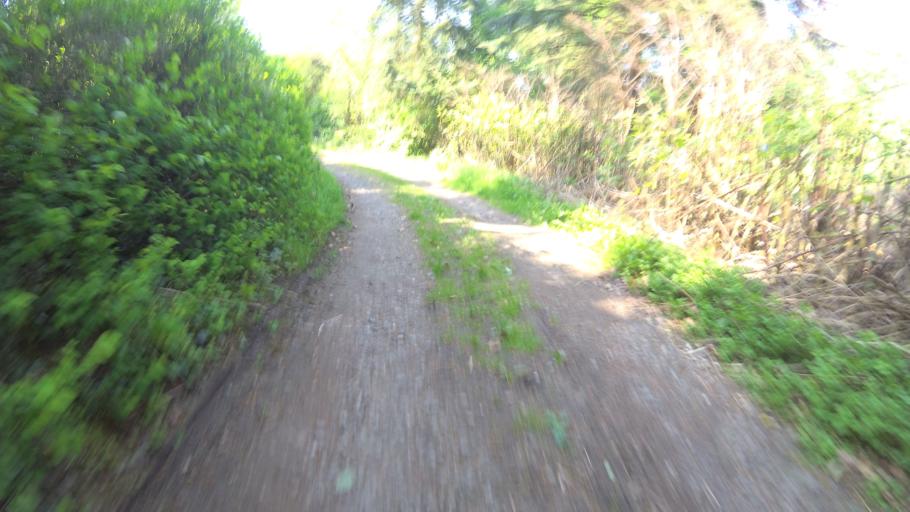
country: DE
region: Saarland
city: Merchweiler
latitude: 49.3531
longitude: 7.0509
